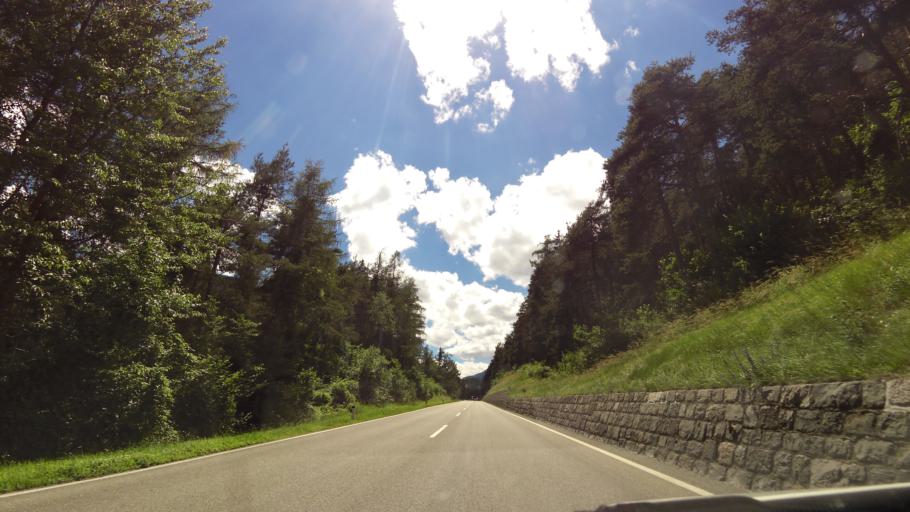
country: AT
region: Tyrol
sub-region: Politischer Bezirk Imst
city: Roppen
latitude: 47.2180
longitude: 10.8069
